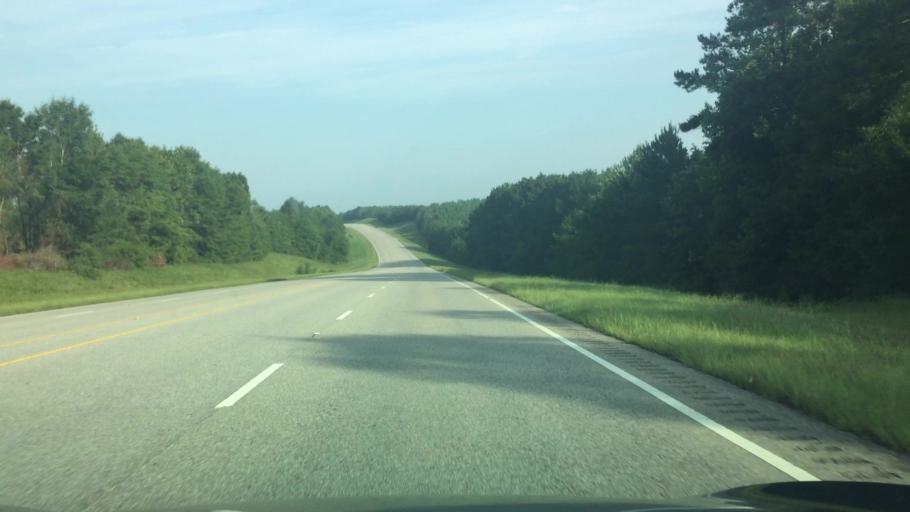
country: US
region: Alabama
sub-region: Butler County
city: Georgiana
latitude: 31.4568
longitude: -86.6363
